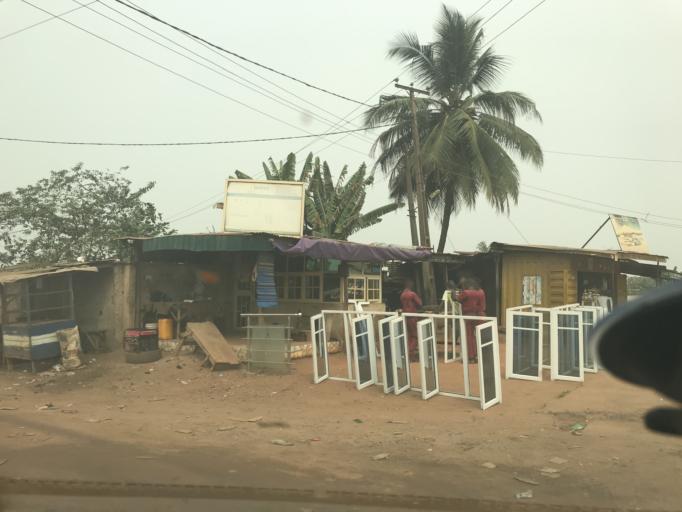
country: NG
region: Ogun
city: Shagamu
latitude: 6.8493
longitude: 3.6315
